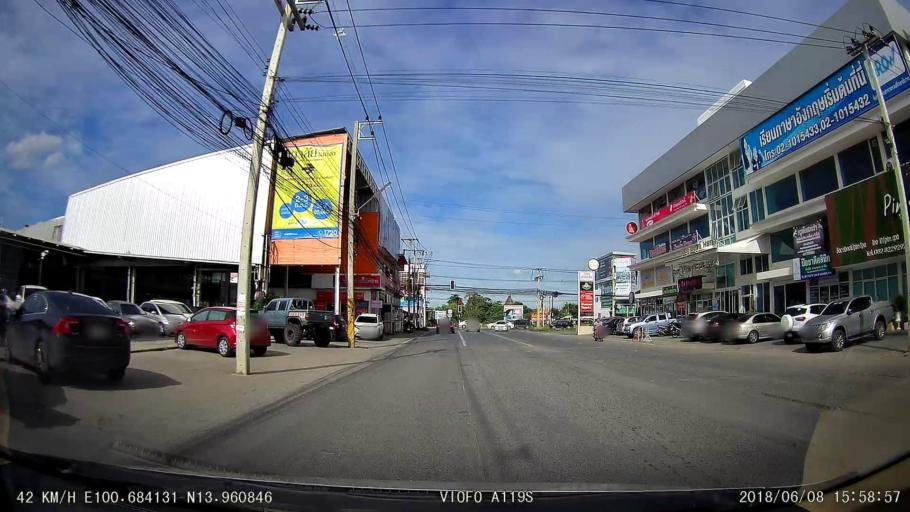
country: TH
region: Bangkok
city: Sai Mai
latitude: 13.9629
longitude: 100.6849
